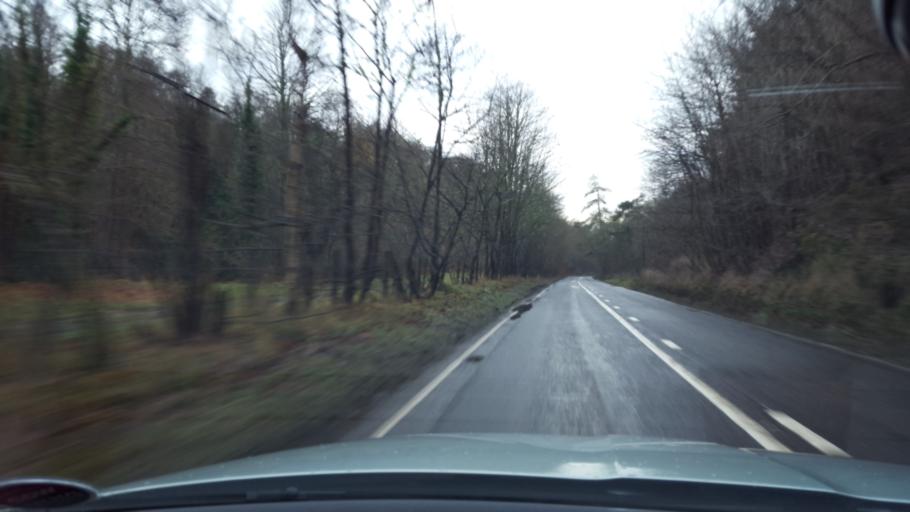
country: GB
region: Scotland
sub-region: Perth and Kinross
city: Bridge of Earn
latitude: 56.2994
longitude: -3.3736
